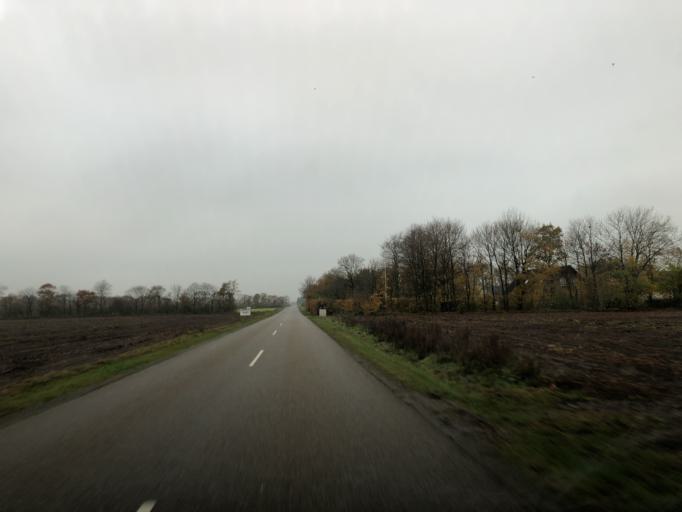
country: DK
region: Central Jutland
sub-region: Herning Kommune
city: Sunds
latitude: 56.2140
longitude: 8.9829
